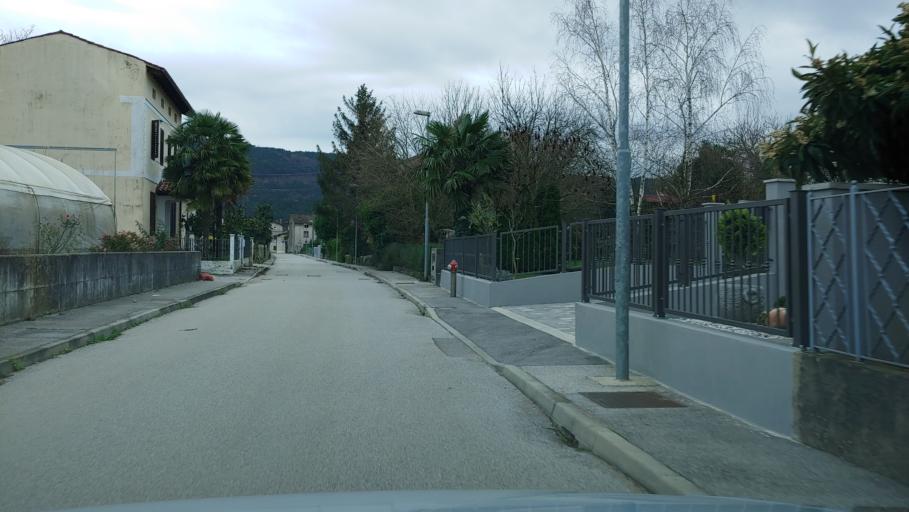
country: SI
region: Miren-Kostanjevica
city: Miren
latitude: 45.8904
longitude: 13.6122
